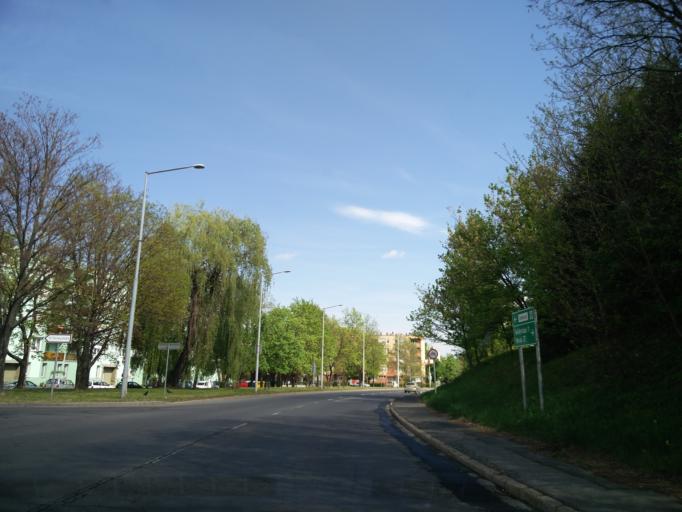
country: HU
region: Zala
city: Zalaegerszeg
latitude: 46.8328
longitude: 16.8282
